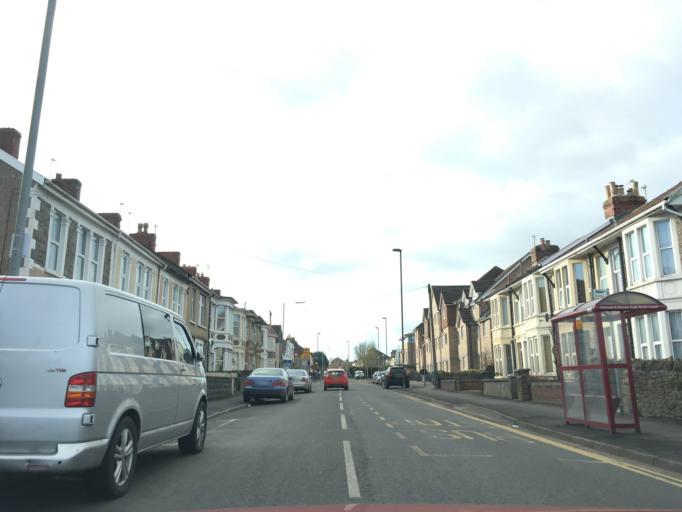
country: GB
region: England
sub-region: South Gloucestershire
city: Mangotsfield
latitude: 51.4864
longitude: -2.5047
